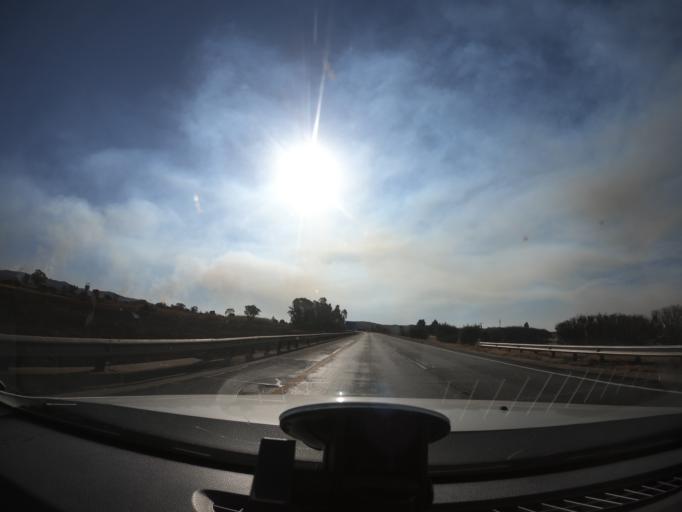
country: ZA
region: Gauteng
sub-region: Sedibeng District Municipality
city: Heidelberg
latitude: -26.4991
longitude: 28.3810
